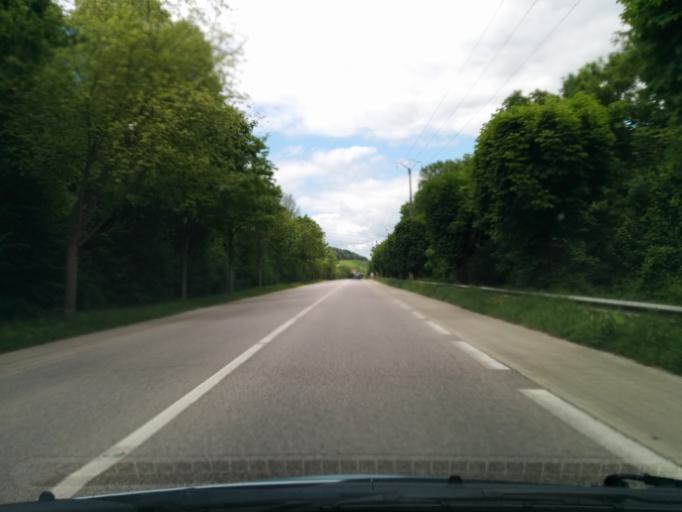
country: FR
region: Ile-de-France
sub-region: Departement des Yvelines
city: Porcheville
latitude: 48.9636
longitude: 1.7638
